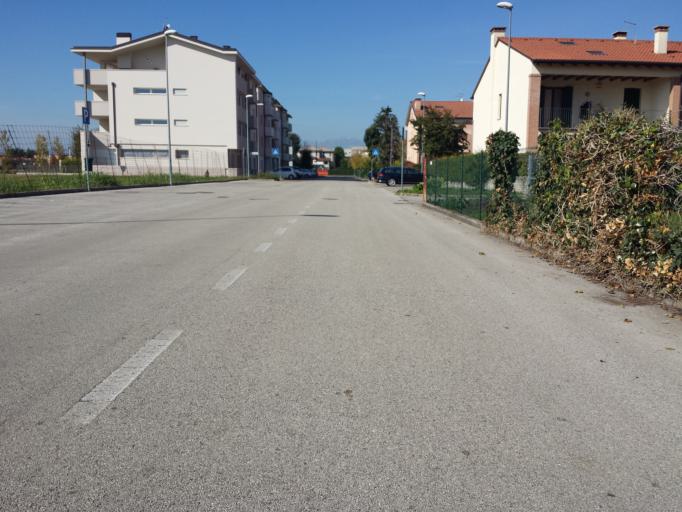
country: IT
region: Veneto
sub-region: Provincia di Vicenza
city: Sandrigo
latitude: 45.6607
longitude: 11.6000
